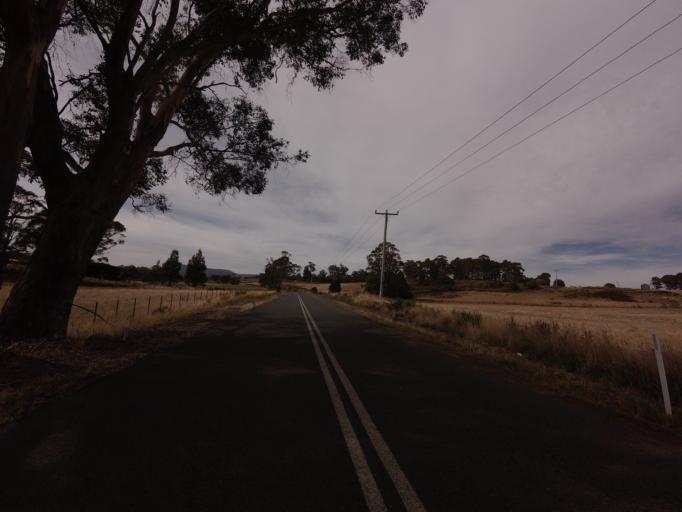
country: AU
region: Tasmania
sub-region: Sorell
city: Sorell
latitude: -42.4141
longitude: 147.4580
